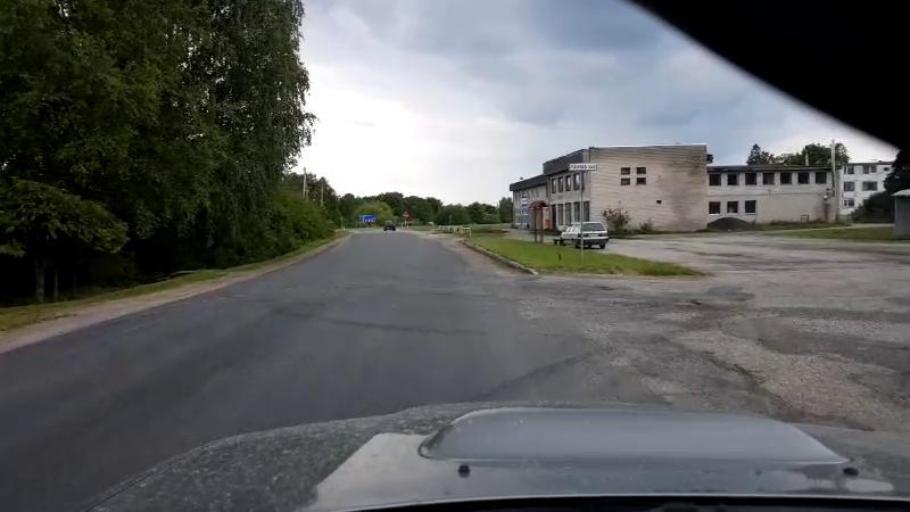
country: EE
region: Paernumaa
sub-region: Tootsi vald
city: Tootsi
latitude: 58.5277
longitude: 24.7023
